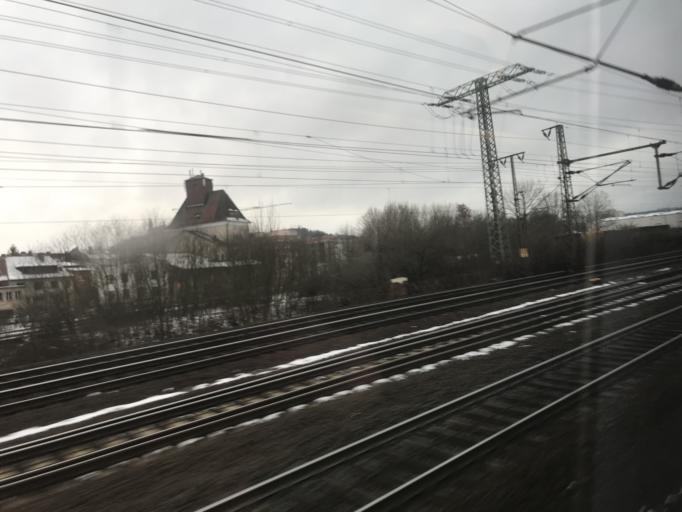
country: DE
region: Hesse
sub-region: Regierungsbezirk Kassel
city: Fulda
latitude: 50.5589
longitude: 9.6797
